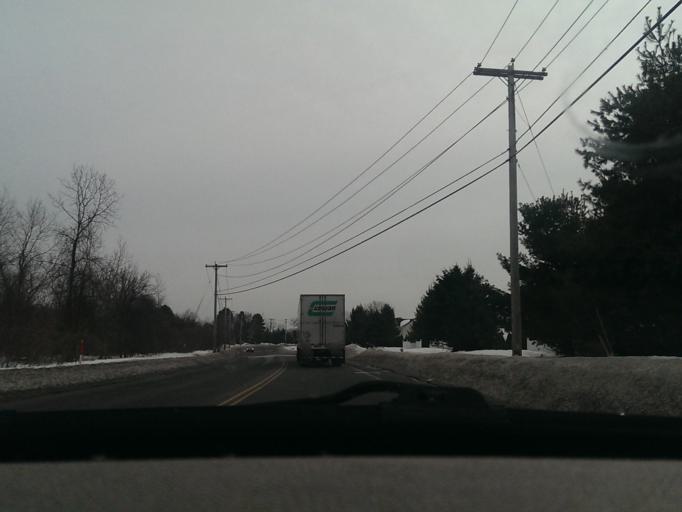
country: US
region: Massachusetts
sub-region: Hampden County
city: East Longmeadow
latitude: 42.0530
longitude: -72.5333
